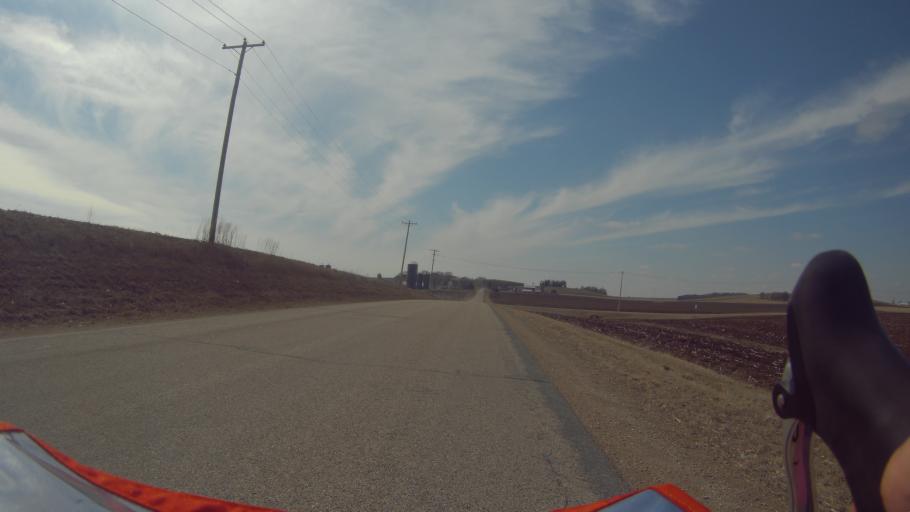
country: US
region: Wisconsin
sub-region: Dane County
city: Waunakee
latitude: 43.1630
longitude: -89.4949
